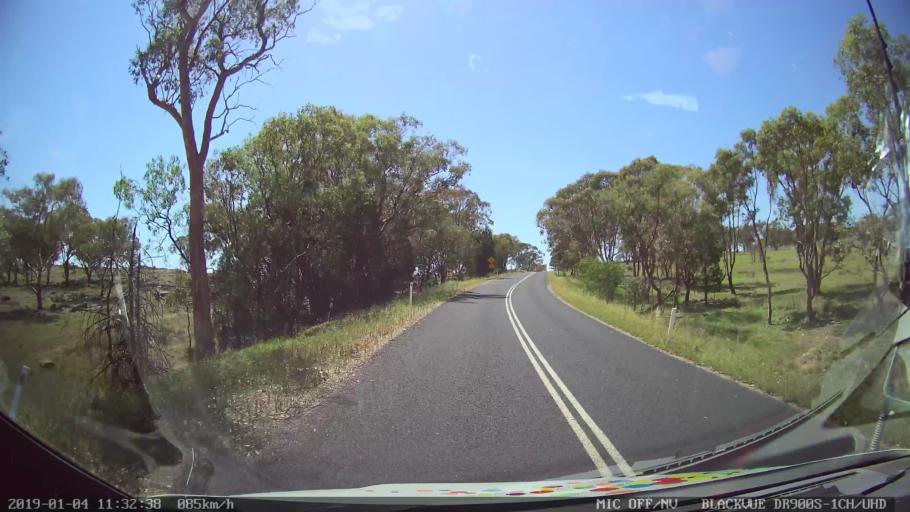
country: AU
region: New South Wales
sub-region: Cabonne
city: Molong
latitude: -33.0626
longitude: 148.8057
